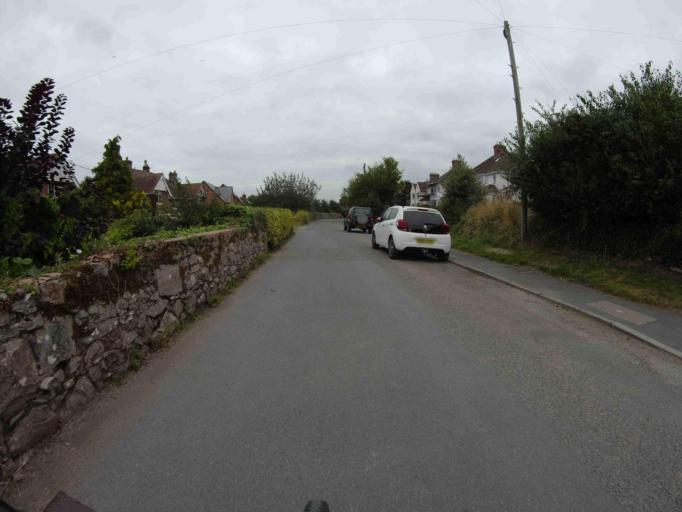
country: GB
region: England
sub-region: Devon
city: Topsham
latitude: 50.6909
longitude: -3.4689
